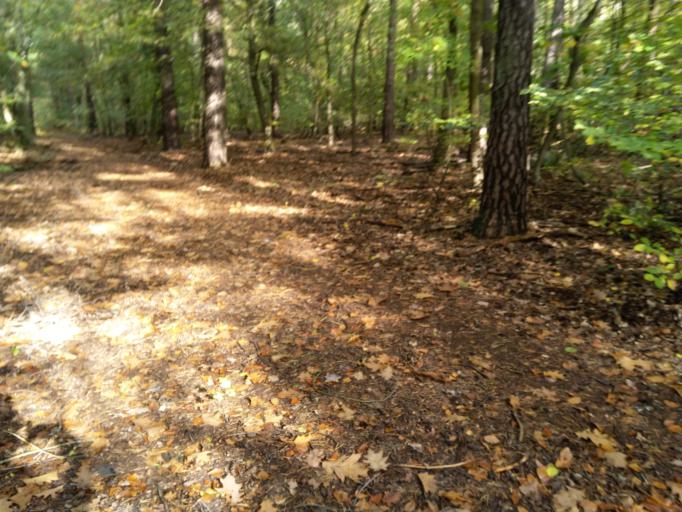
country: DE
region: Berlin
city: Rahnsdorf
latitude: 52.4499
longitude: 13.6778
